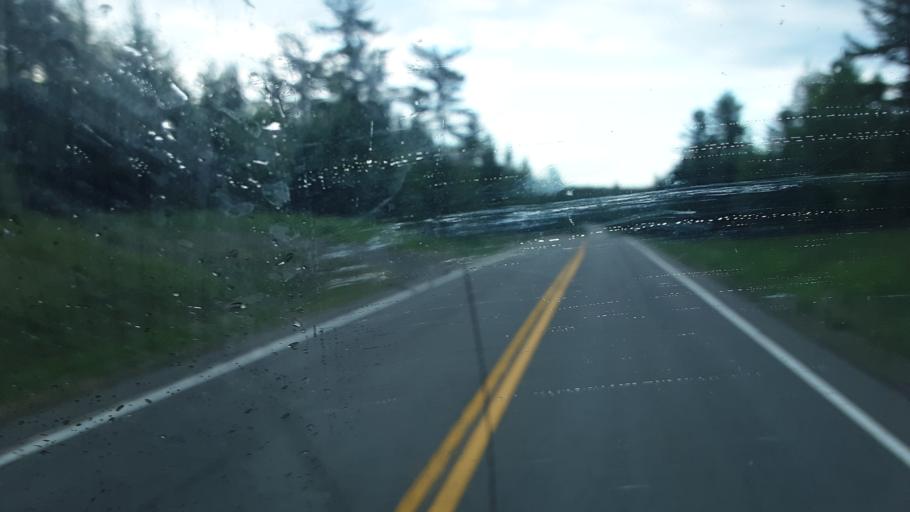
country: US
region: Maine
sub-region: Penobscot County
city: Patten
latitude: 46.4179
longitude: -68.3735
